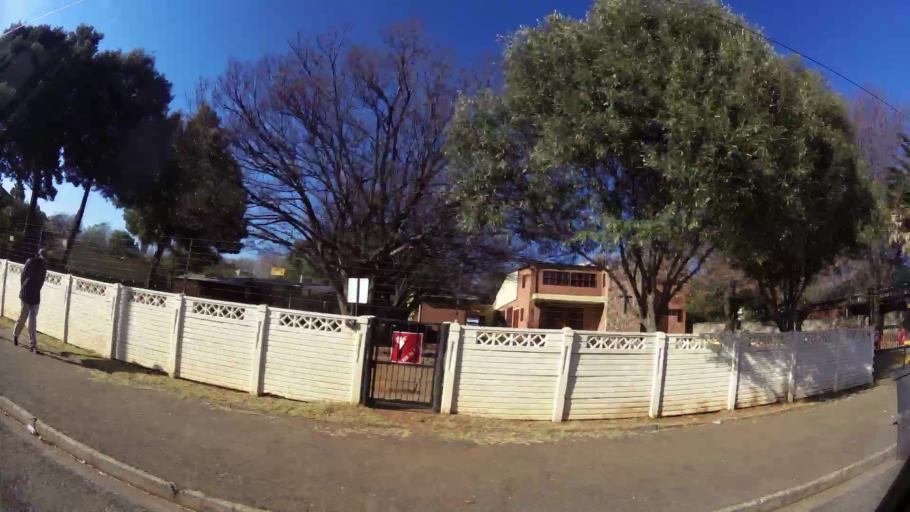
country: ZA
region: Gauteng
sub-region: City of Johannesburg Metropolitan Municipality
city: Johannesburg
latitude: -26.1879
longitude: 28.1050
